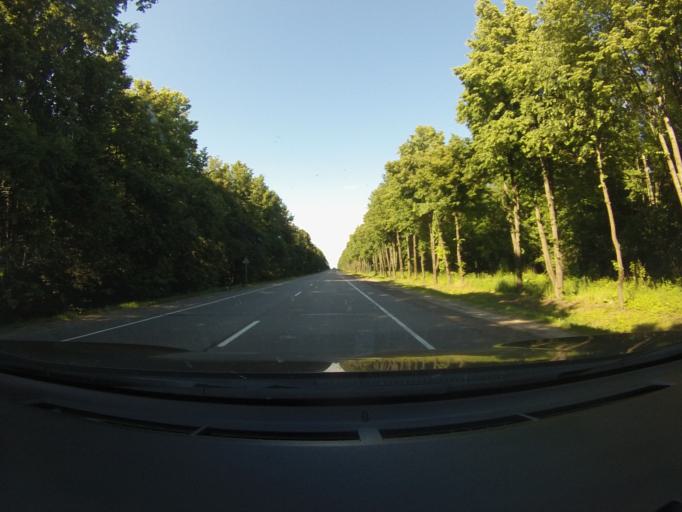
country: RU
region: Orjol
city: Spasskoye-Lutovinovo
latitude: 53.3559
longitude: 36.7196
